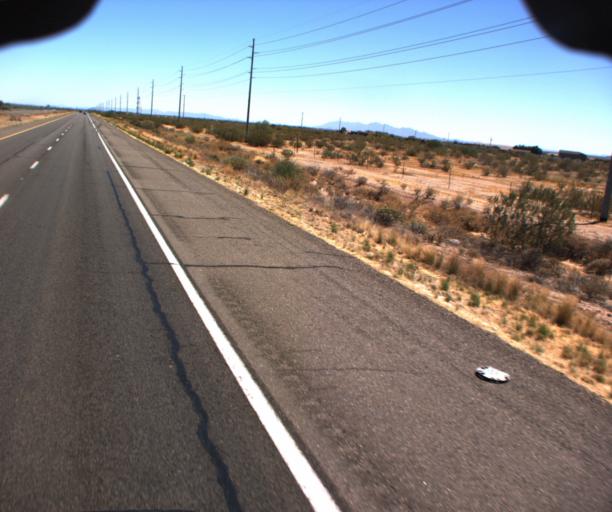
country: US
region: Arizona
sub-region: Maricopa County
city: Sun City West
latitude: 33.7526
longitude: -112.4965
